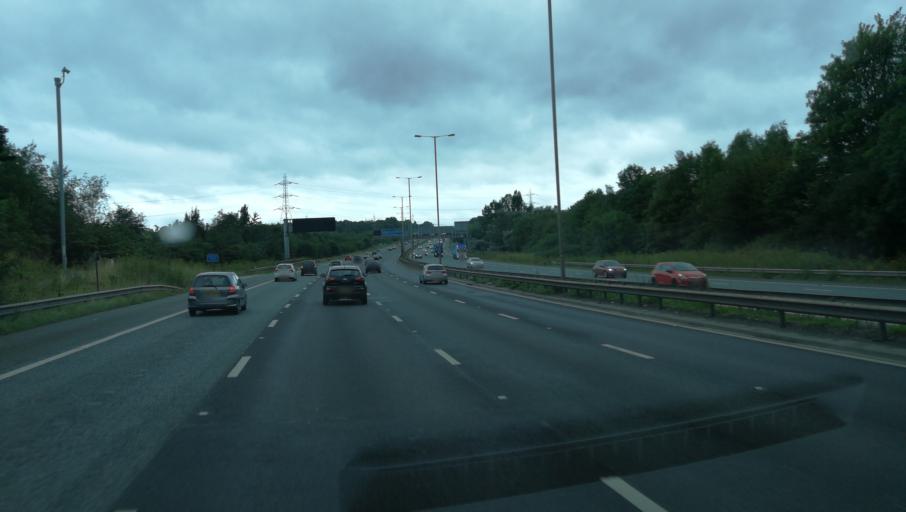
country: GB
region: England
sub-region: Borough of Bury
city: Whitefield
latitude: 53.5307
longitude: -2.3172
